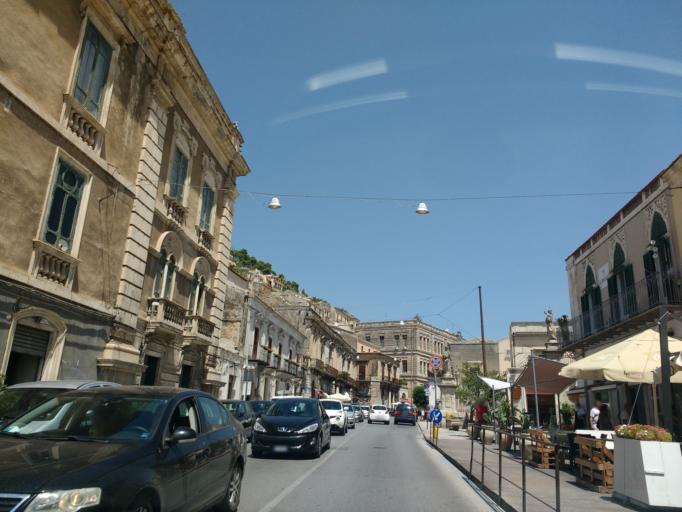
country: IT
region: Sicily
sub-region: Ragusa
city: Modica
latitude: 36.8600
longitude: 14.7603
